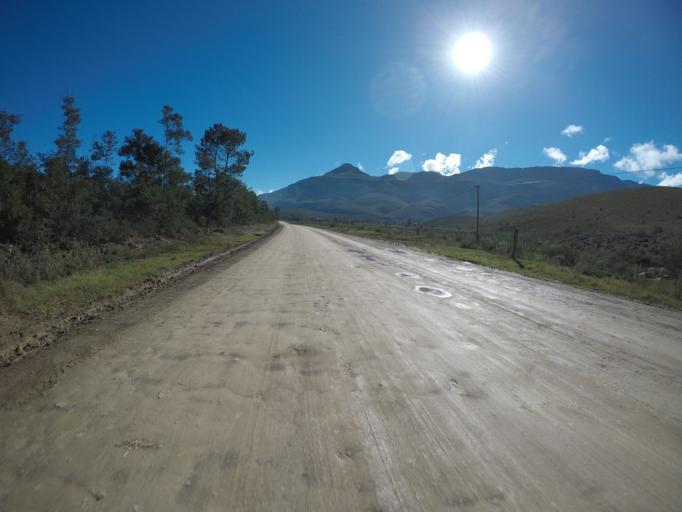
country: ZA
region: Western Cape
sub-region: Overberg District Municipality
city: Caledon
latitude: -34.0587
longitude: 19.6213
